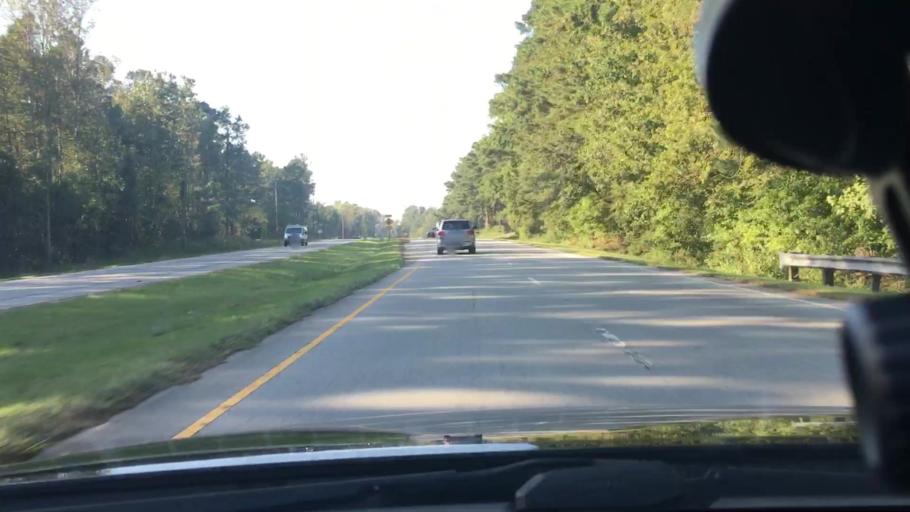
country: US
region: North Carolina
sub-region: Craven County
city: Vanceboro
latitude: 35.2839
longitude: -77.1254
